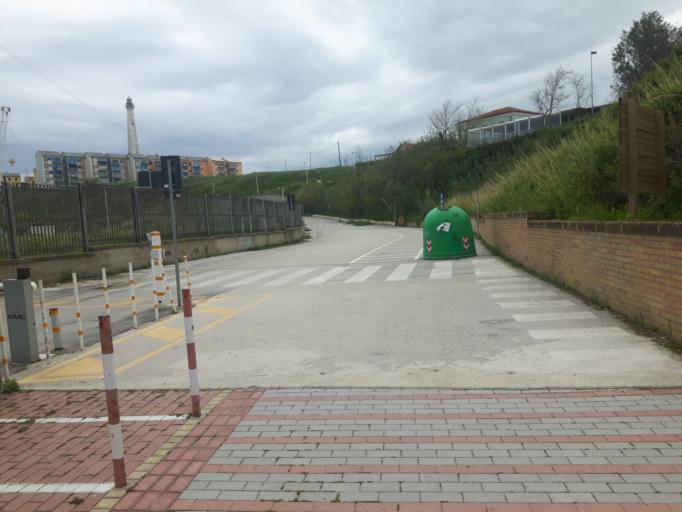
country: IT
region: Abruzzo
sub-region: Provincia di Chieti
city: Vasto
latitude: 42.1716
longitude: 14.7102
